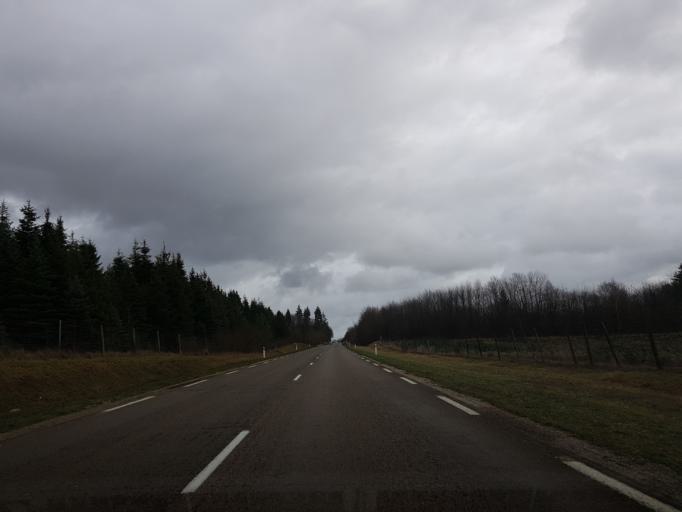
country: FR
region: Franche-Comte
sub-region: Departement de la Haute-Saone
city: Scey-sur-Saone-et-Saint-Albin
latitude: 47.6988
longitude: 5.9541
